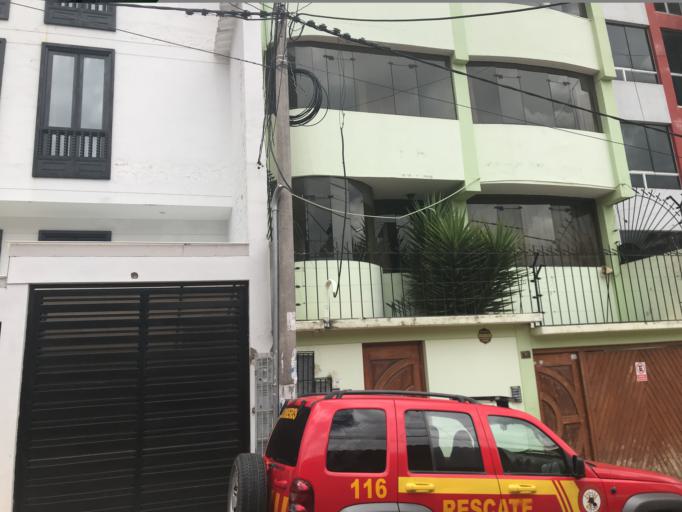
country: PE
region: Cusco
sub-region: Provincia de Cusco
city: Cusco
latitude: -13.5184
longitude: -71.9652
